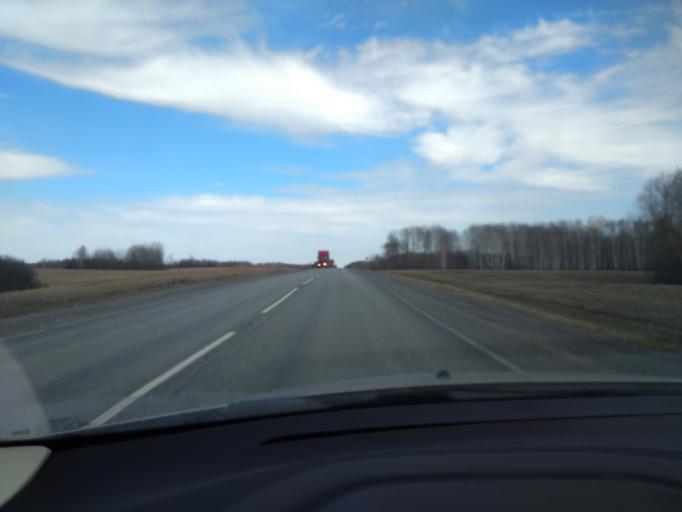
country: RU
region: Sverdlovsk
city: Pyshma
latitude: 56.9987
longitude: 63.3004
